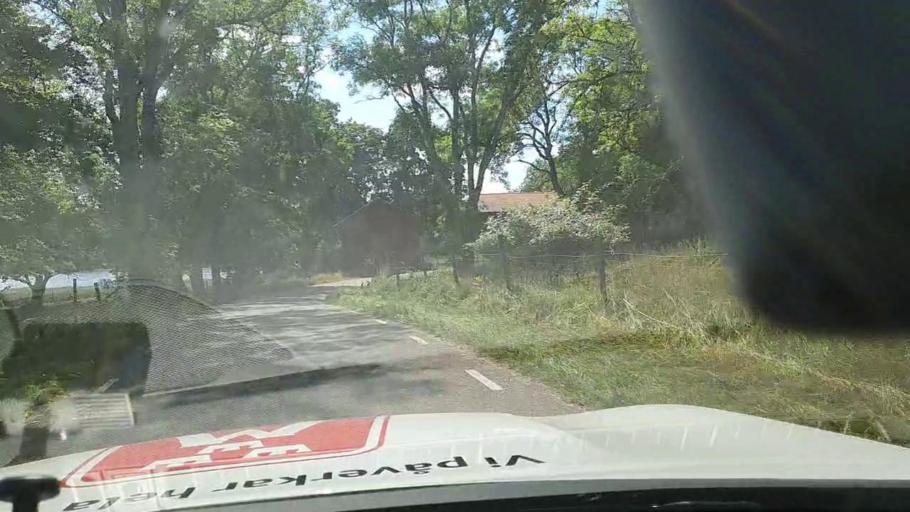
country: SE
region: Soedermanland
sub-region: Strangnas Kommun
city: Akers Styckebruk
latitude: 59.2727
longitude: 16.9845
